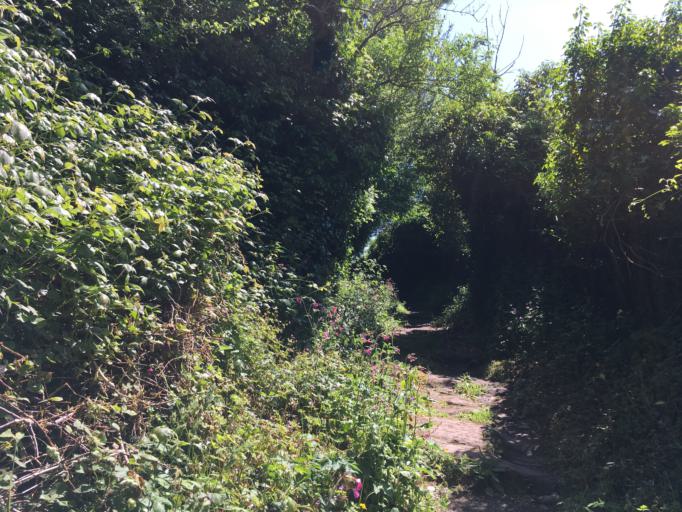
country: GB
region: England
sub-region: Devon
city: Dartmouth
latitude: 50.3452
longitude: -3.5498
